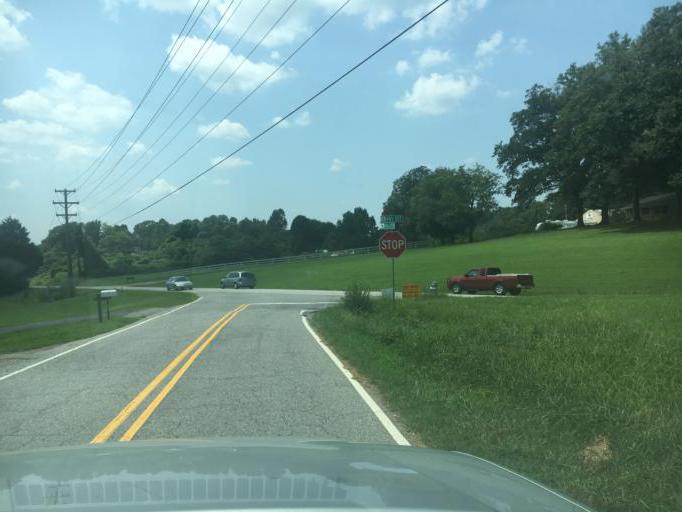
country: US
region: South Carolina
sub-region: Greenville County
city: Greer
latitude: 34.9623
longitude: -82.2015
